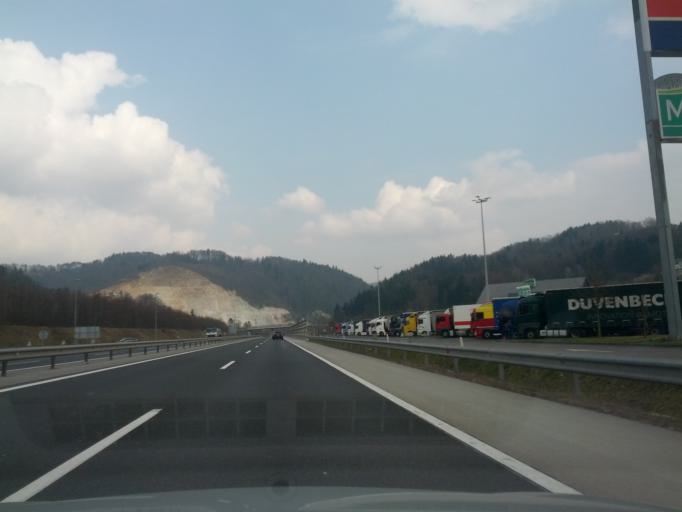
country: SI
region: Lukovica
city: Lukovica pri Domzalah
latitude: 46.1671
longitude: 14.6927
